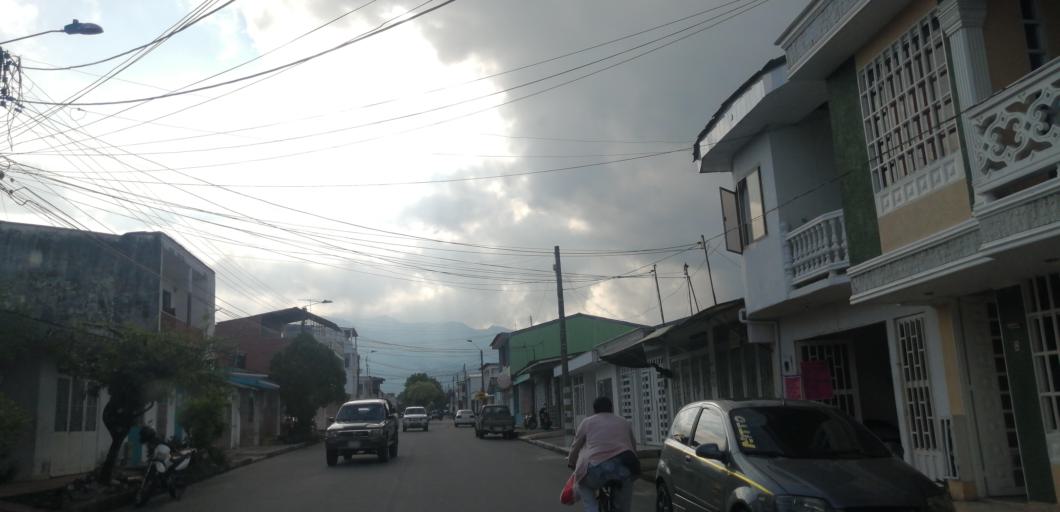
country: CO
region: Meta
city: Acacias
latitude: 3.9859
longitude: -73.7709
